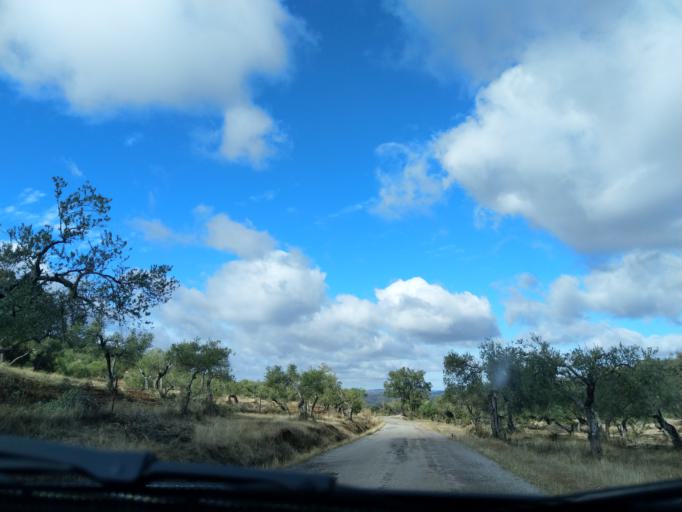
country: ES
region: Extremadura
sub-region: Provincia de Badajoz
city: Reina
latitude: 38.1294
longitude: -5.9358
